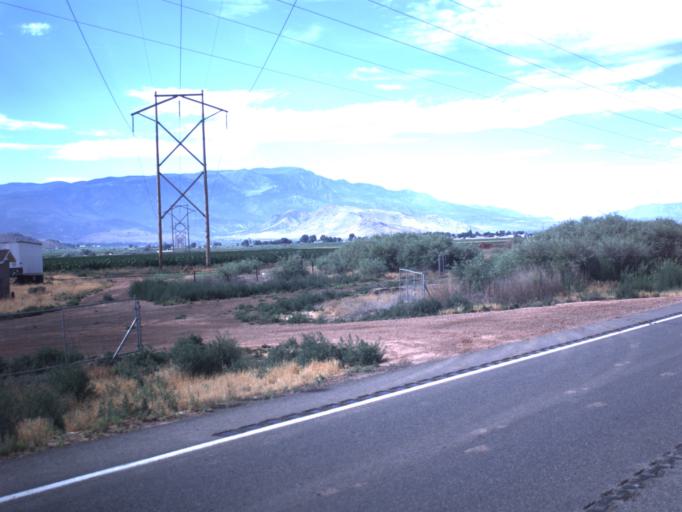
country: US
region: Utah
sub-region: Sevier County
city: Richfield
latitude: 38.8254
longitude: -111.9967
